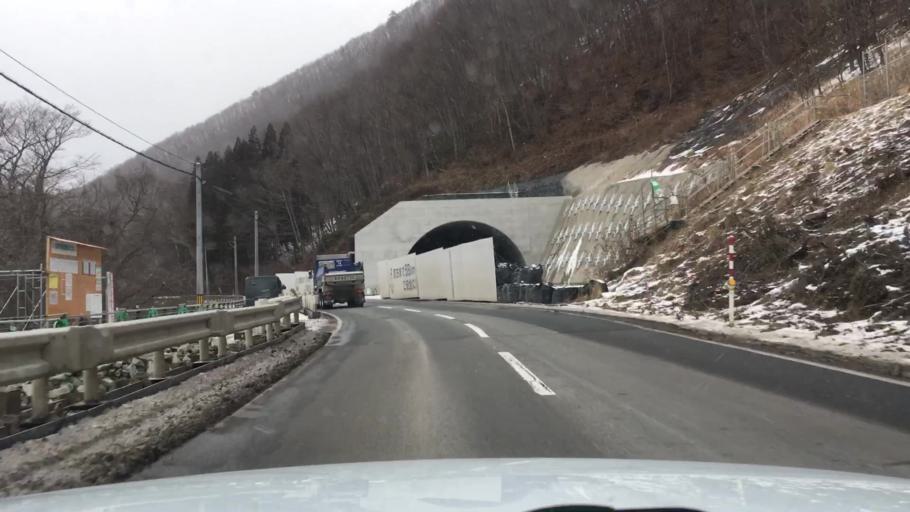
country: JP
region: Iwate
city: Tono
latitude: 39.6256
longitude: 141.4691
